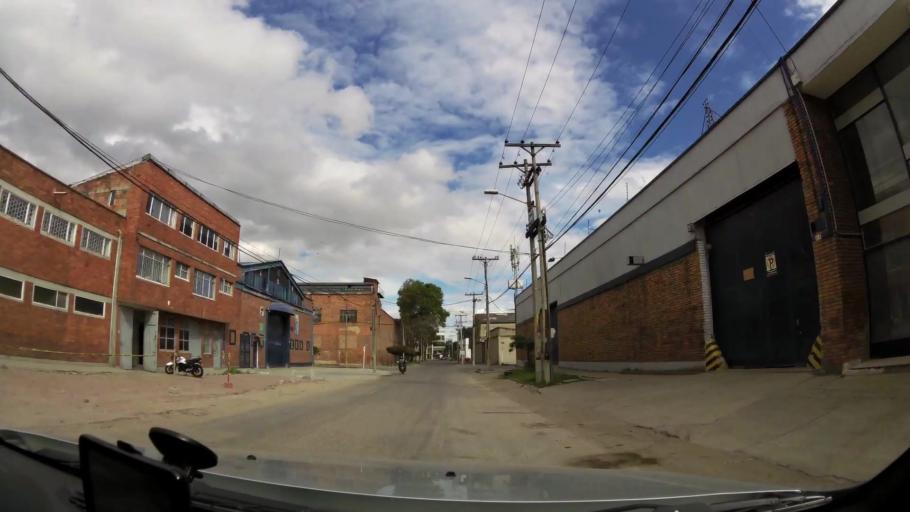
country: CO
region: Bogota D.C.
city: Bogota
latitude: 4.6246
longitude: -74.0994
